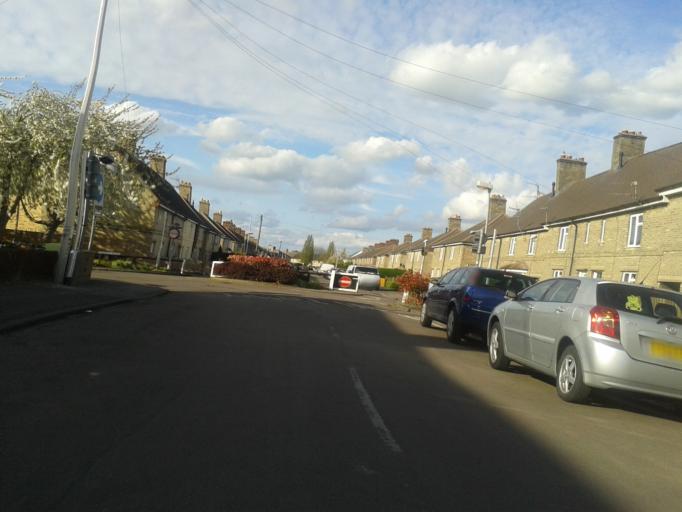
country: GB
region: England
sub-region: Cambridgeshire
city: Cambridge
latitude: 52.2018
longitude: 0.1505
